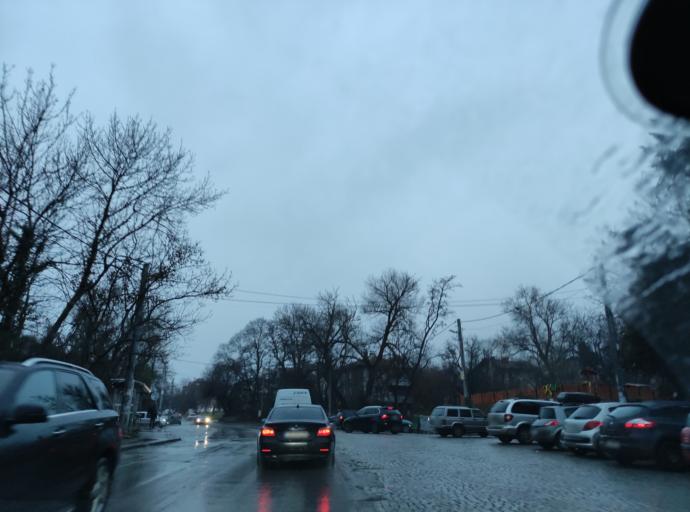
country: BG
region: Sofia-Capital
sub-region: Stolichna Obshtina
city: Sofia
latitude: 42.6339
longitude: 23.3107
